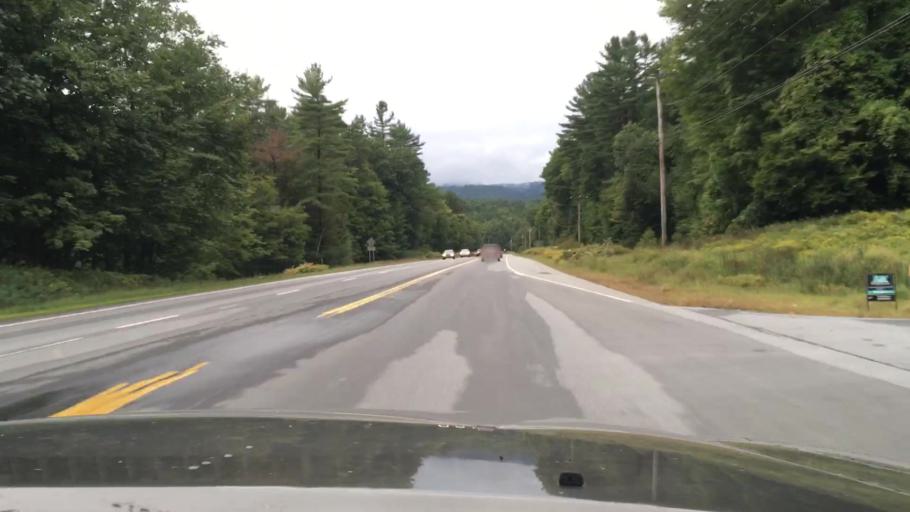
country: US
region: New Hampshire
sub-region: Cheshire County
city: Chesterfield
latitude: 42.8931
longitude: -72.5018
